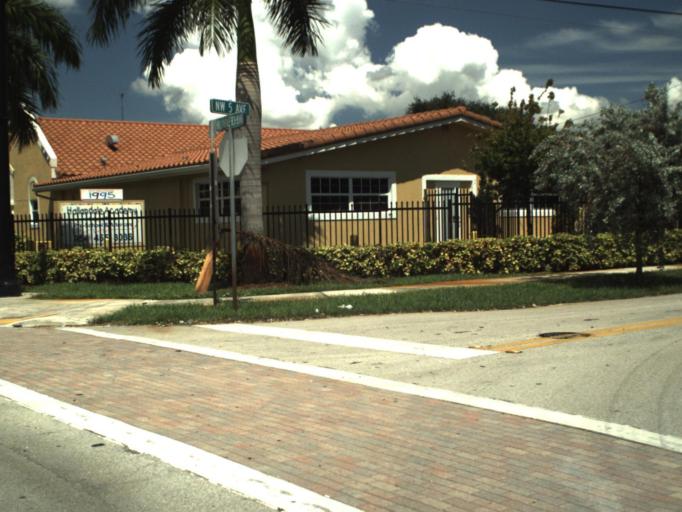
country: US
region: Florida
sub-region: Broward County
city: Hallandale Beach
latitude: 25.9855
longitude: -80.1532
